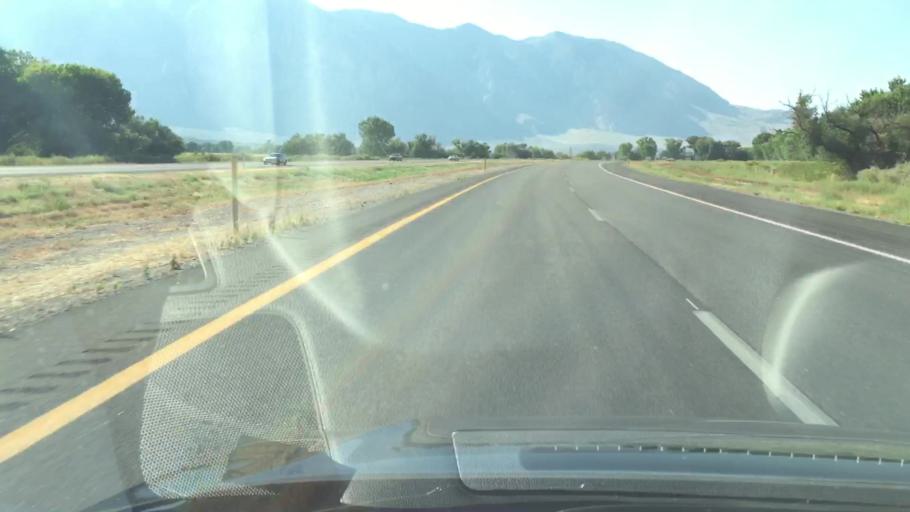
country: US
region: California
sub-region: Inyo County
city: West Bishop
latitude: 37.4077
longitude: -118.5468
